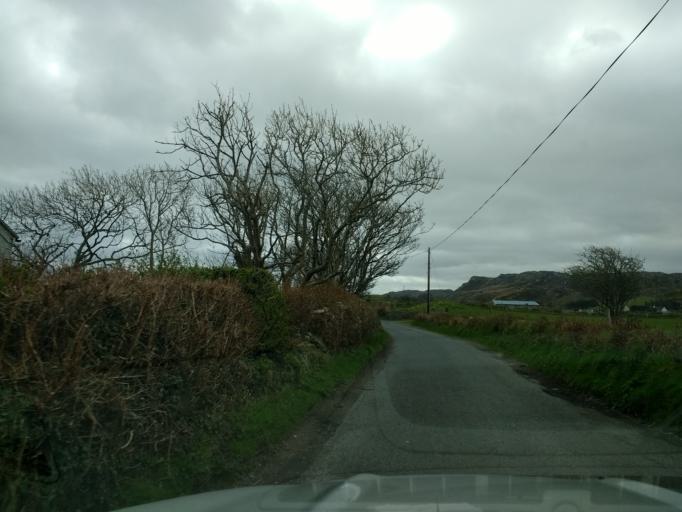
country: IE
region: Ulster
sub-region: County Donegal
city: Buncrana
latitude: 55.2486
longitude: -7.6228
